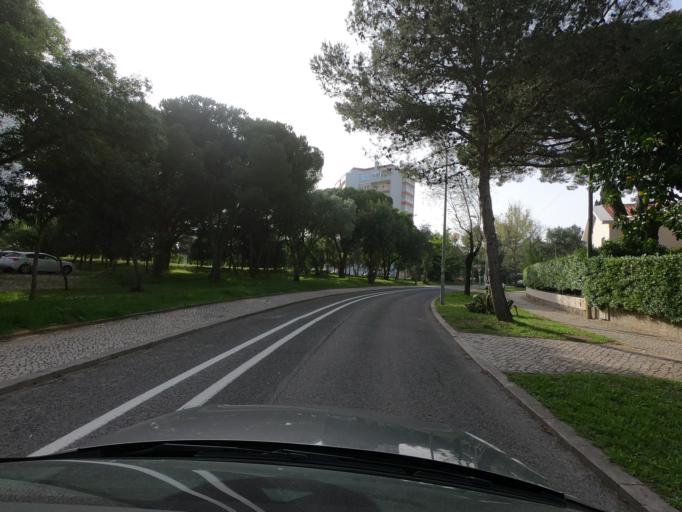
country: PT
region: Lisbon
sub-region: Oeiras
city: Carcavelos
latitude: 38.6926
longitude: -9.3213
